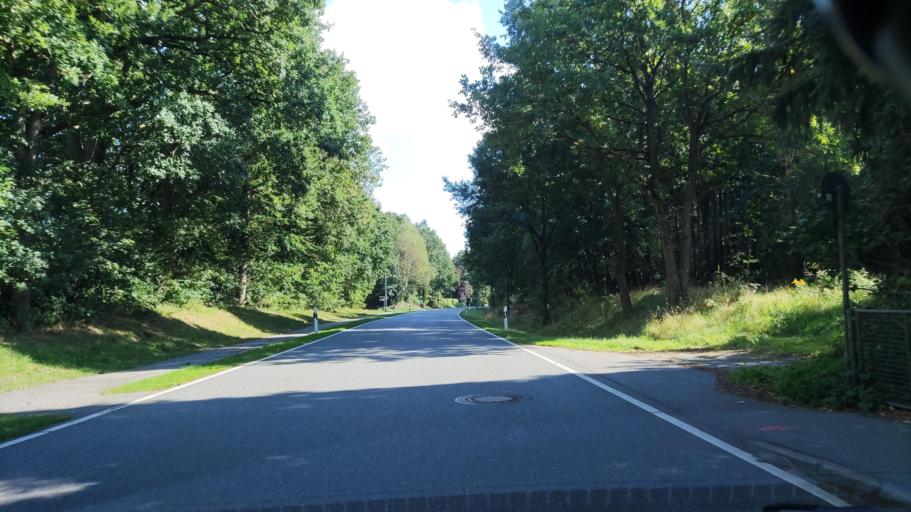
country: DE
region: Schleswig-Holstein
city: Luhnstedt
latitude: 54.2079
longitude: 9.7101
